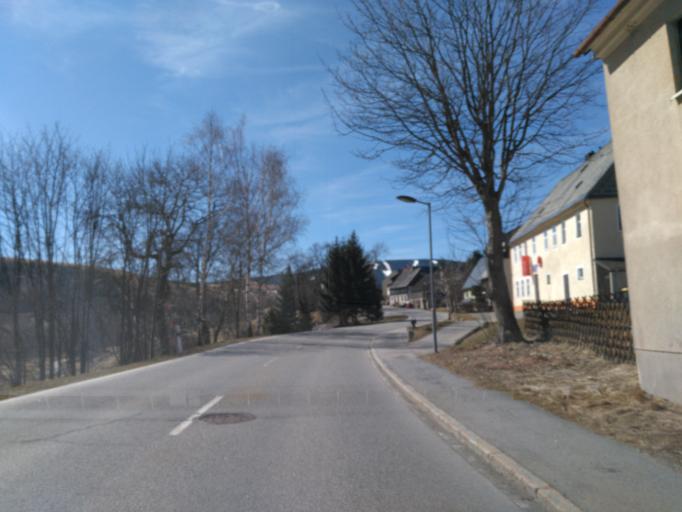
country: DE
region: Saxony
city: Kurort Oberwiesenthal
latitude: 50.4276
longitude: 12.9884
